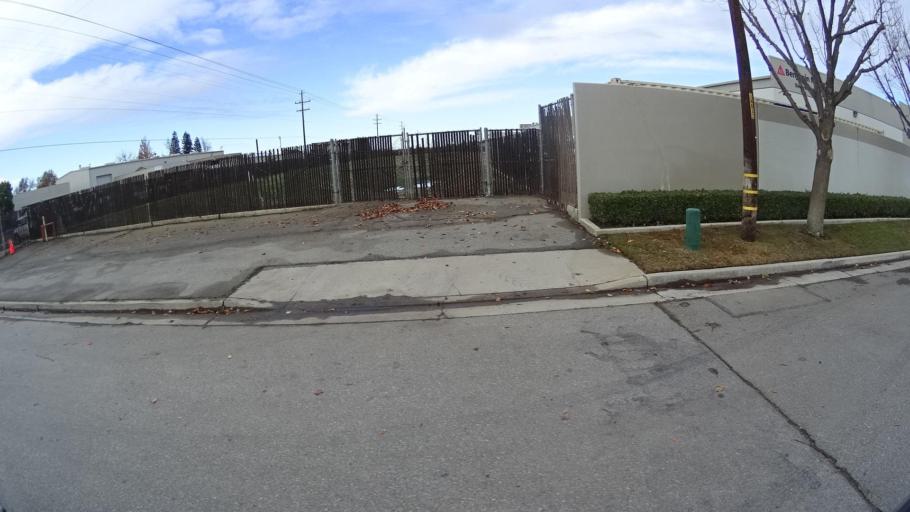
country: US
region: California
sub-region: Kern County
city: Bakersfield
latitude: 35.3907
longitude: -119.0591
